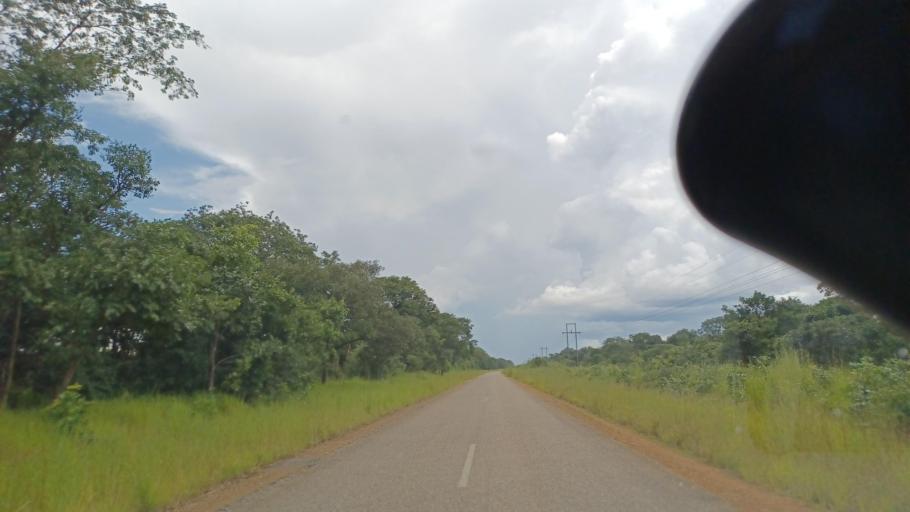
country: ZM
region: North-Western
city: Kasempa
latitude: -13.1397
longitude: 25.8773
